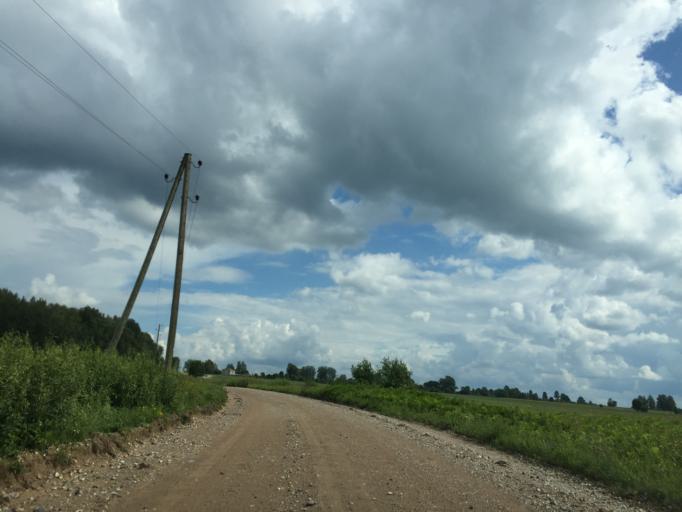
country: LV
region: Ligatne
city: Ligatne
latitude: 57.2154
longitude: 24.9491
